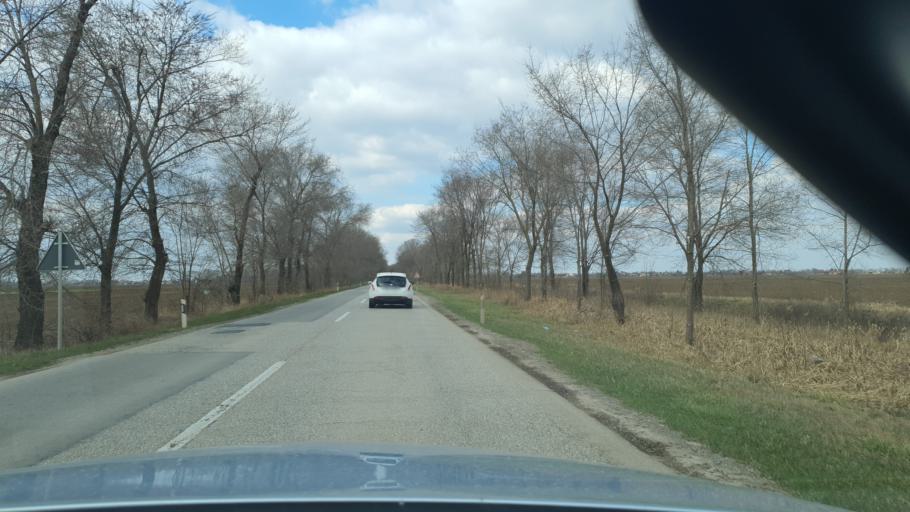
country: RS
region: Autonomna Pokrajina Vojvodina
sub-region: Zapadnobacki Okrug
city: Odzaci
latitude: 45.4442
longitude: 19.3651
